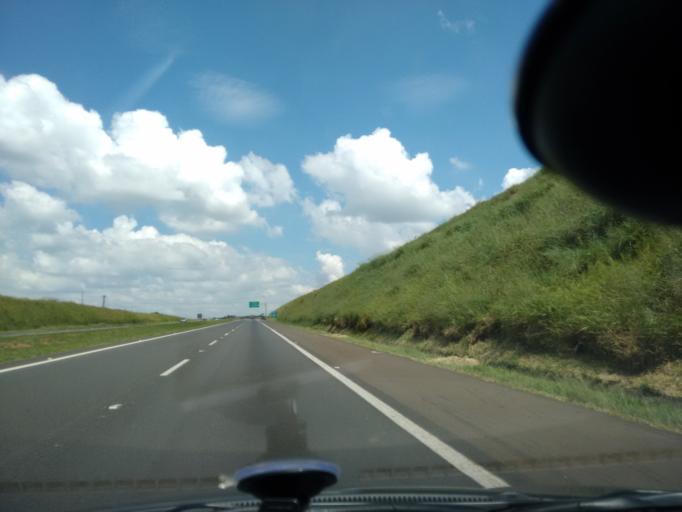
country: BR
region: Sao Paulo
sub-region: Santa Barbara D'Oeste
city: Santa Barbara d'Oeste
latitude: -22.7540
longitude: -47.4454
